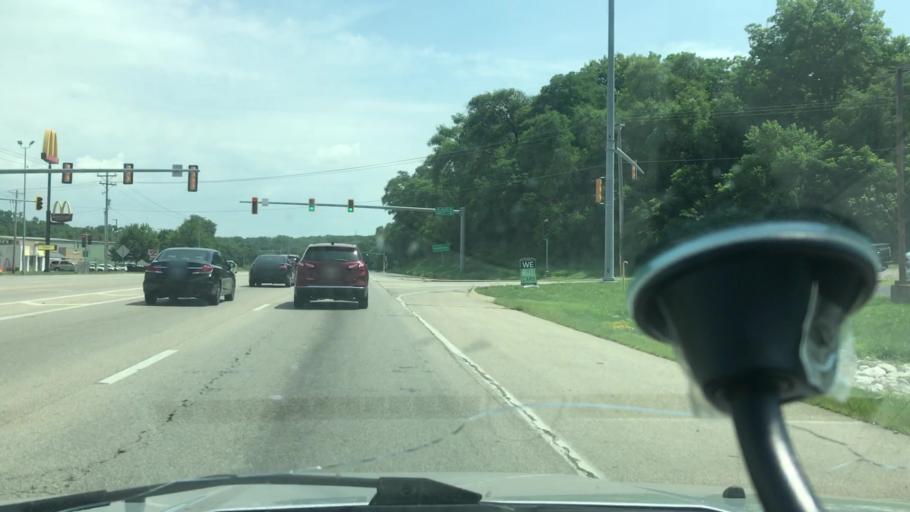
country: US
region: Illinois
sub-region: Tazewell County
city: North Pekin
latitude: 40.6250
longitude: -89.6196
